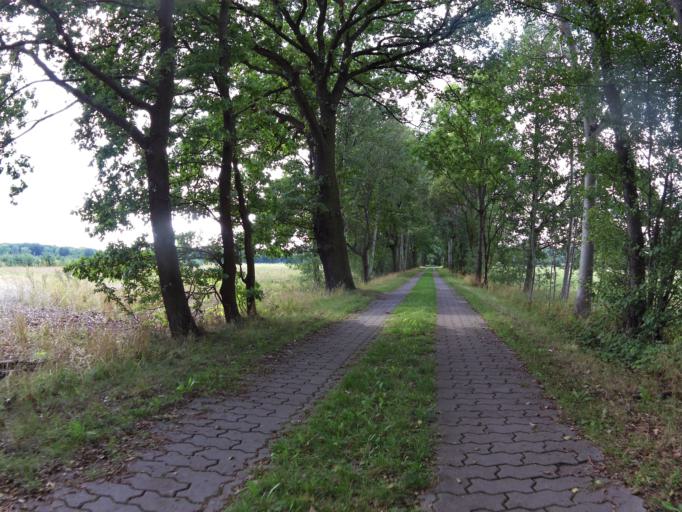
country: DE
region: Brandenburg
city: Storkow
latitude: 52.2364
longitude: 13.8782
